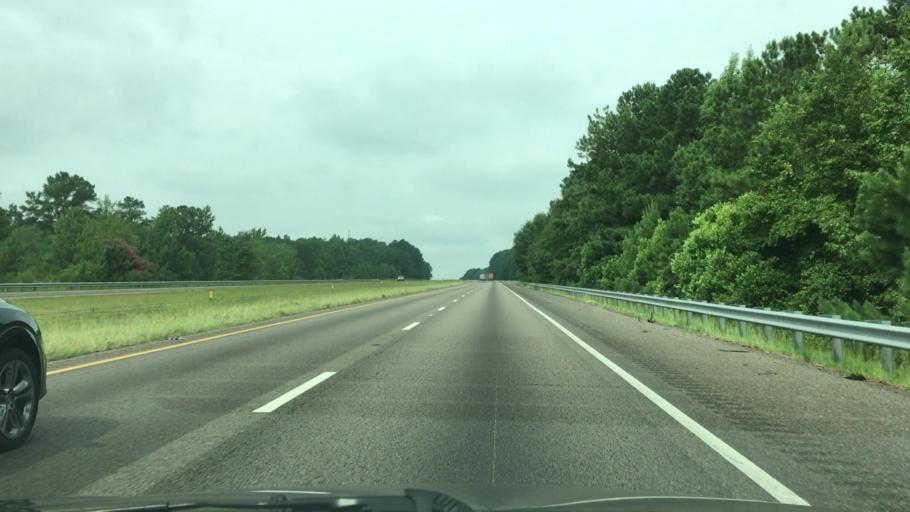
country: US
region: South Carolina
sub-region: Edgefield County
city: Murphys Estates
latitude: 33.5826
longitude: -81.8918
